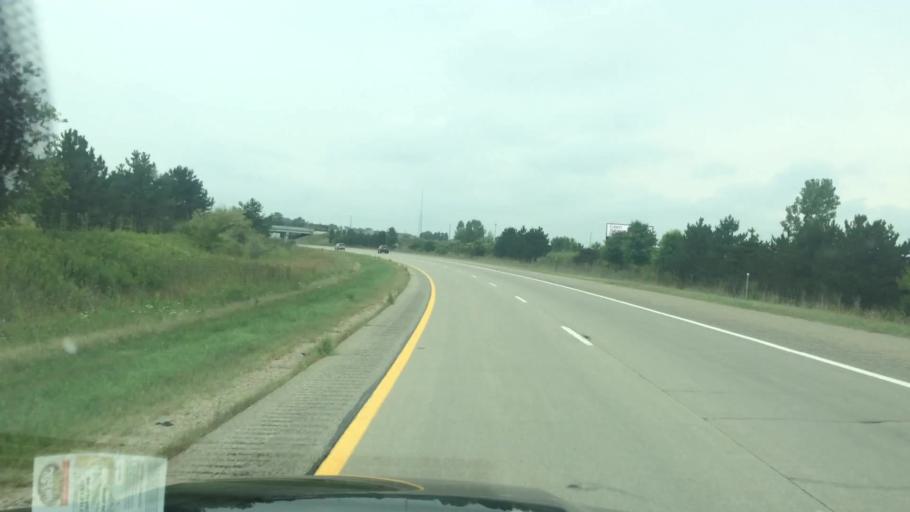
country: US
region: Michigan
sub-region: Eaton County
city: Dimondale
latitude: 42.6942
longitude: -84.6658
